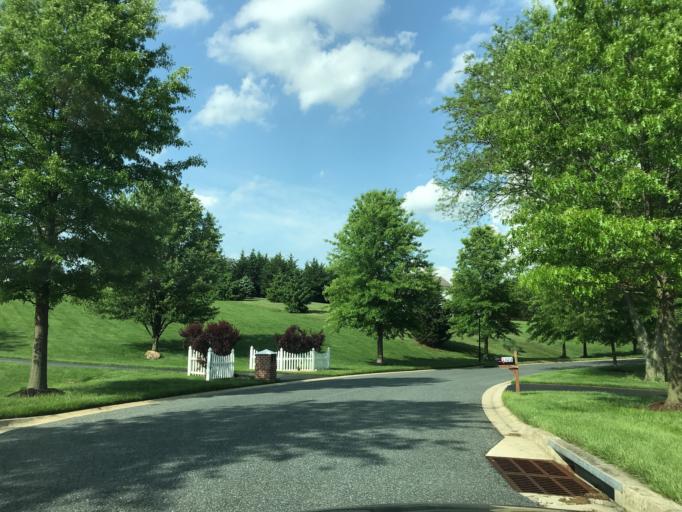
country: US
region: Maryland
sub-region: Harford County
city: Bel Air North
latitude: 39.5541
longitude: -76.3952
